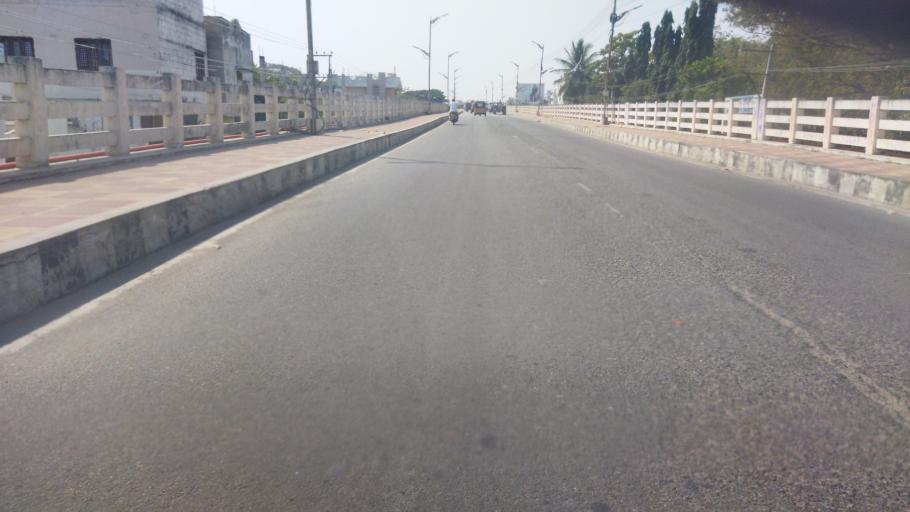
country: IN
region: Telangana
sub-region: Nalgonda
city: Nalgonda
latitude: 17.0673
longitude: 79.2812
